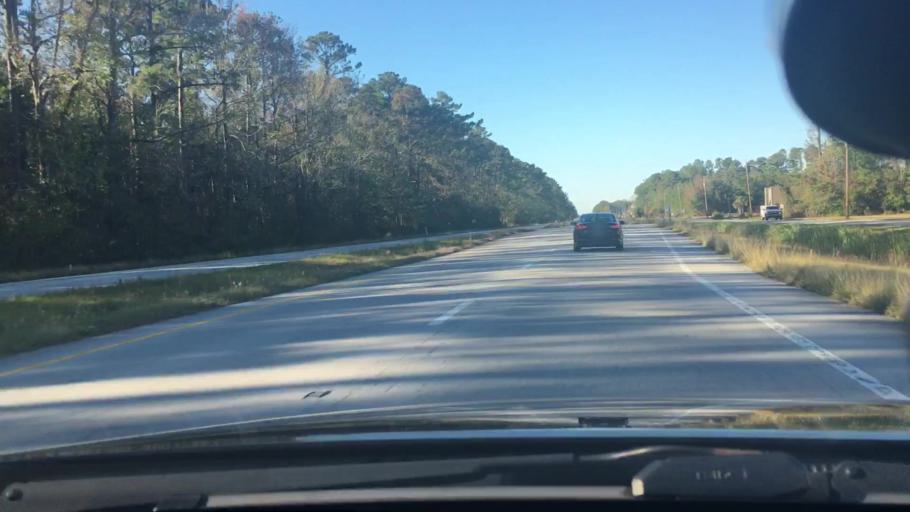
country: US
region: North Carolina
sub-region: Craven County
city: Fairfield Harbour
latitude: 35.0298
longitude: -77.0026
